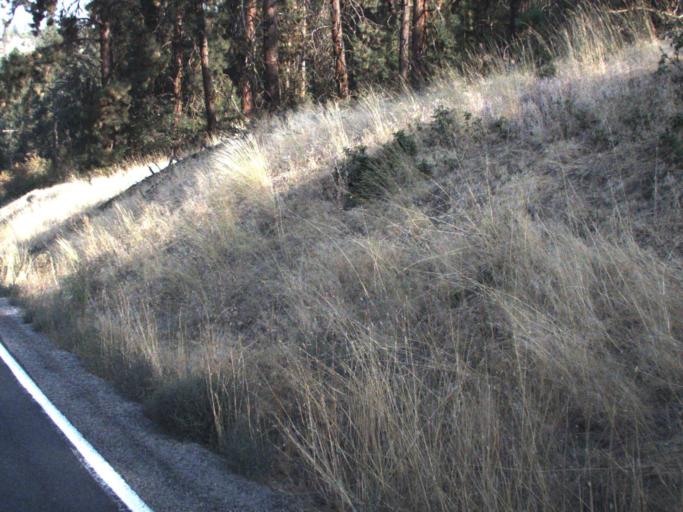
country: US
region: Washington
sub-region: Spokane County
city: Fairwood
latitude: 47.7939
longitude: -117.5318
